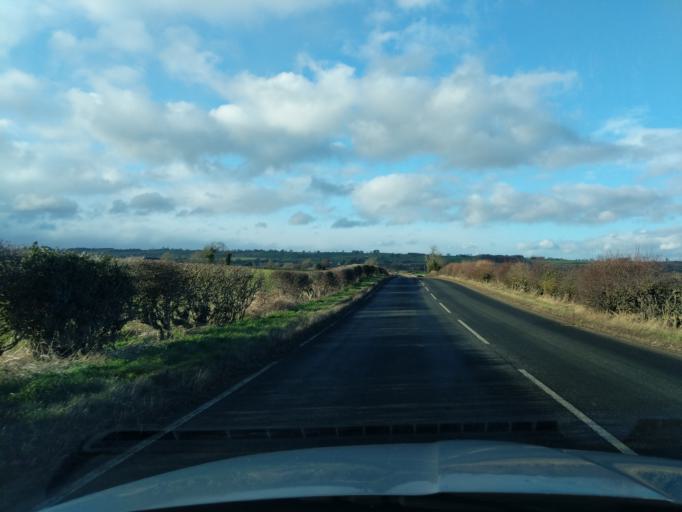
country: GB
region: England
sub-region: North Yorkshire
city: Catterick Garrison
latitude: 54.3218
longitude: -1.6798
